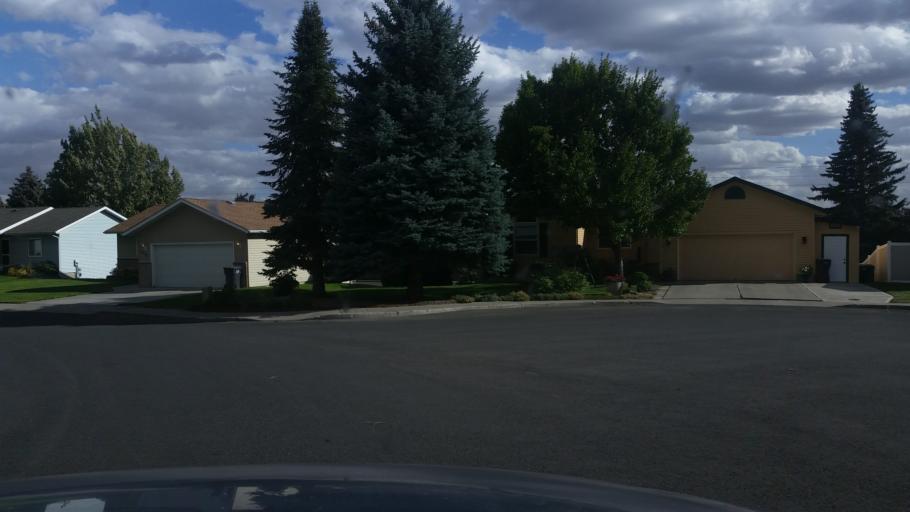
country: US
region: Washington
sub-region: Spokane County
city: Cheney
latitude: 47.4827
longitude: -117.6017
